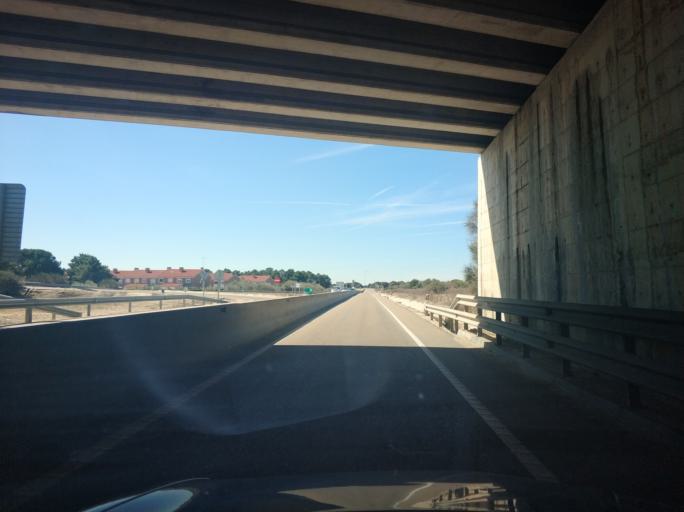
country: ES
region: Castille and Leon
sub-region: Provincia de Valladolid
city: Boecillo
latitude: 41.5366
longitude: -4.7041
